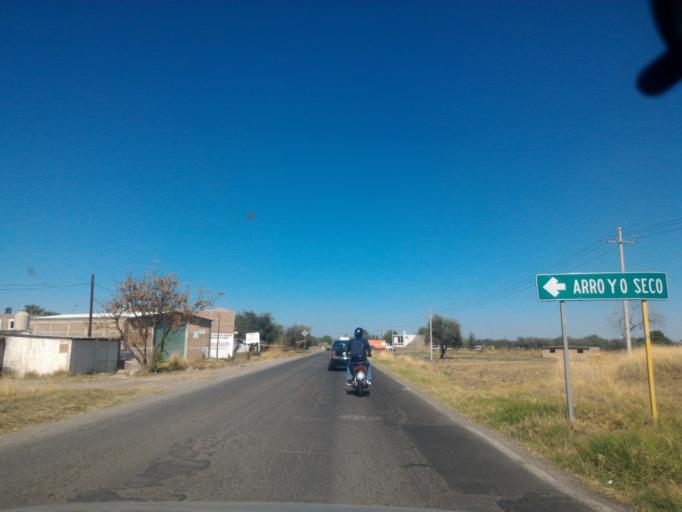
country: MX
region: Guanajuato
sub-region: San Francisco del Rincon
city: San Roque de Montes
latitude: 20.9963
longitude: -101.8144
